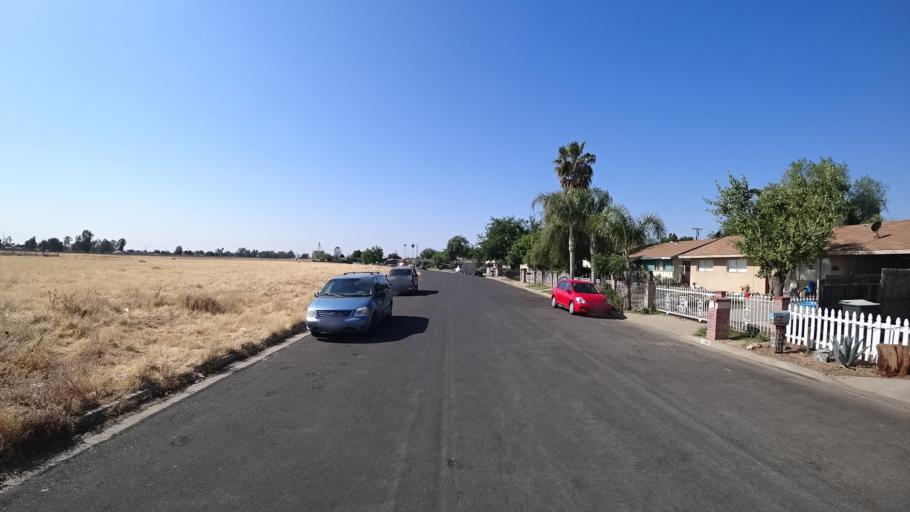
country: US
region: California
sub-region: Kings County
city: Home Garden
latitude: 36.3079
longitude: -119.6515
